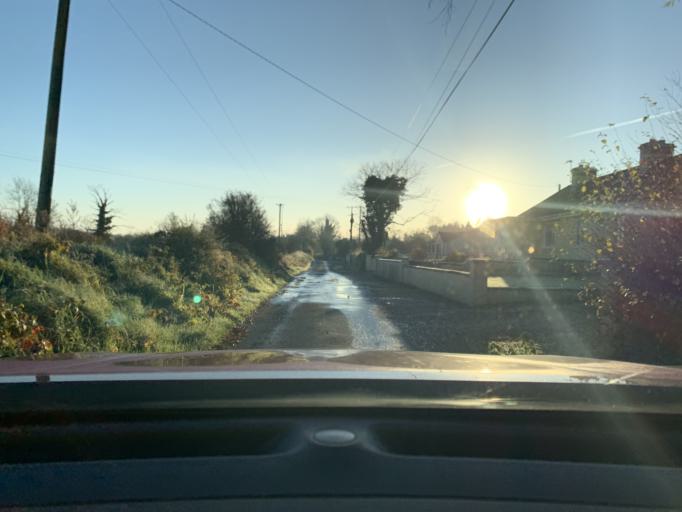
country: IE
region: Connaught
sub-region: Sligo
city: Ballymote
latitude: 53.9867
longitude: -8.5250
